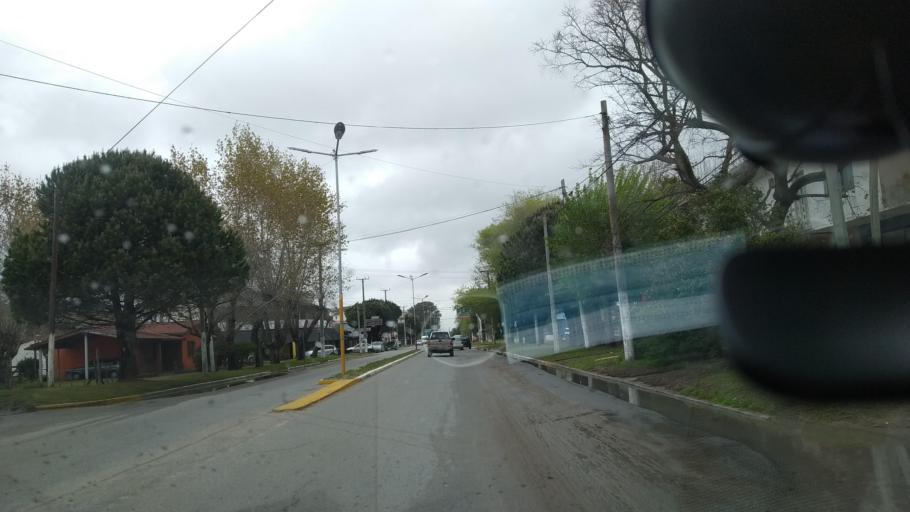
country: AR
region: Buenos Aires
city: San Clemente del Tuyu
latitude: -36.3735
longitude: -56.7181
